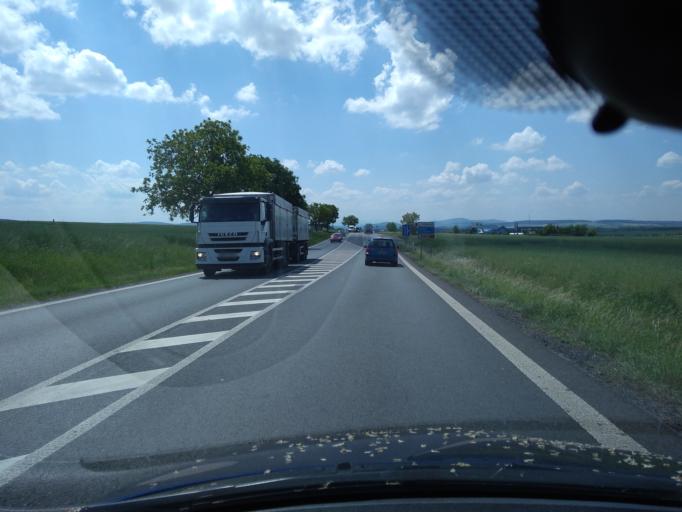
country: CZ
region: Plzensky
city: Chlumcany
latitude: 49.6316
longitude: 13.3320
